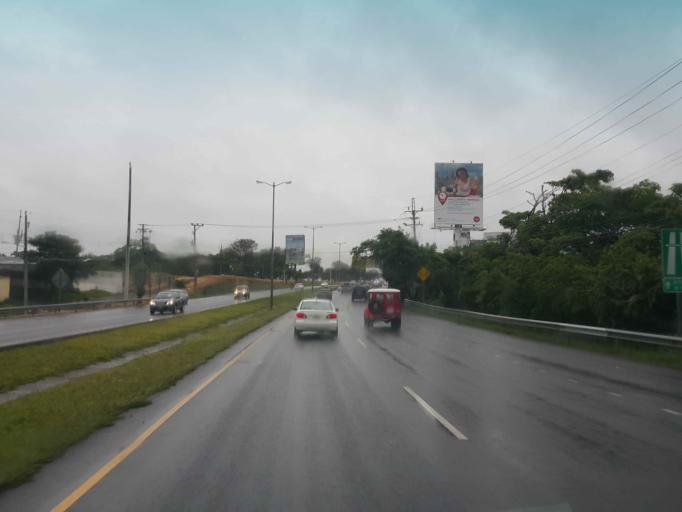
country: CR
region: San Jose
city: Santa Ana
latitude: 9.9476
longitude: -84.1603
